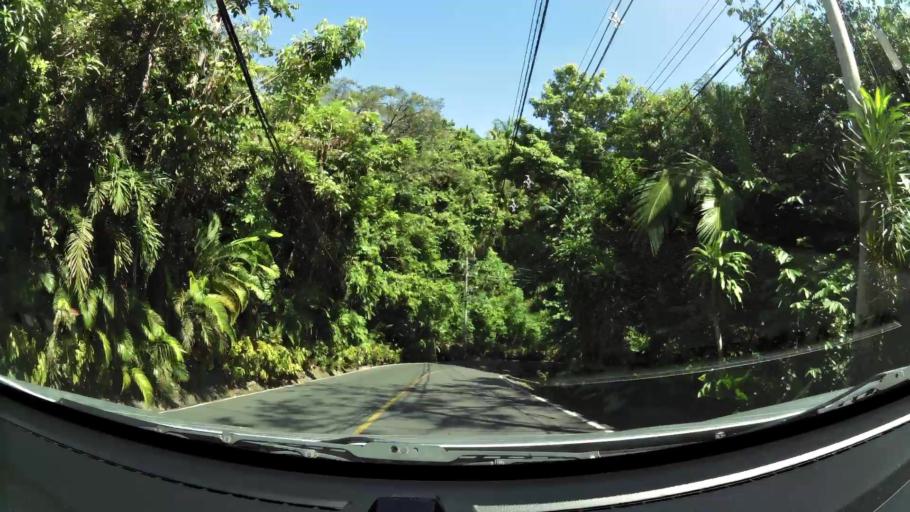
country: CR
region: Puntarenas
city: Quepos
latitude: 9.3978
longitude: -84.1549
